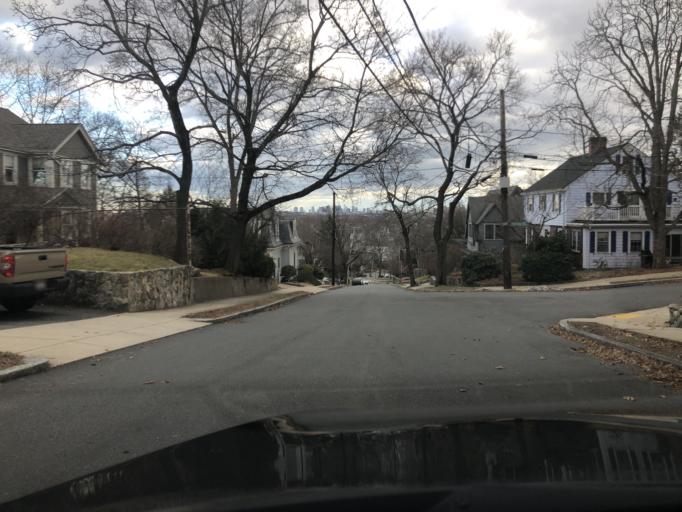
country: US
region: Massachusetts
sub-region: Middlesex County
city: Arlington
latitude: 42.4100
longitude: -71.1610
